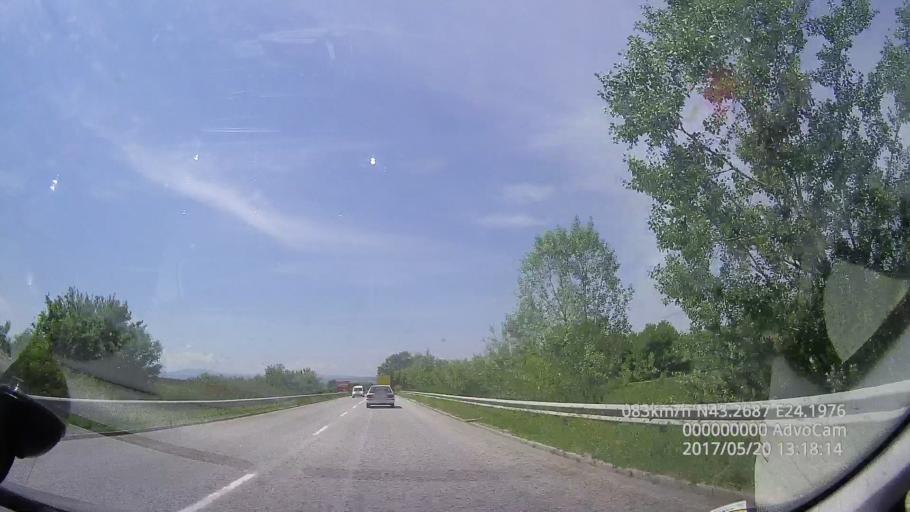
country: BG
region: Lovech
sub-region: Obshtina Lukovit
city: Lukovit
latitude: 43.2682
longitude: 24.1970
